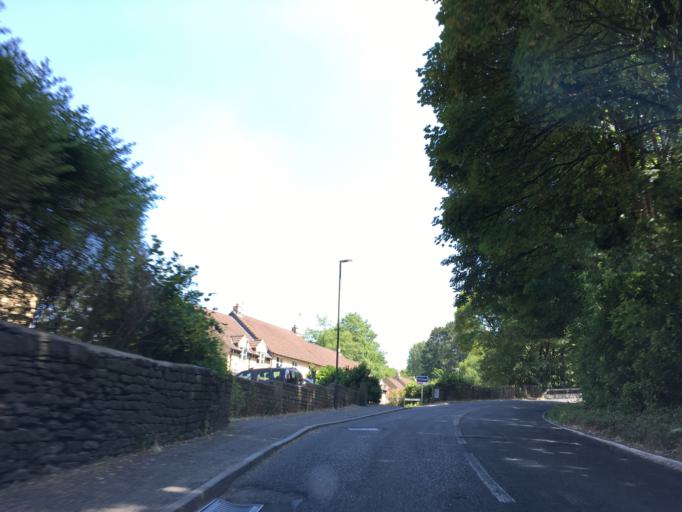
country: GB
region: England
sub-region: Gloucestershire
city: Chalford
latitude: 51.7210
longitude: -2.1507
